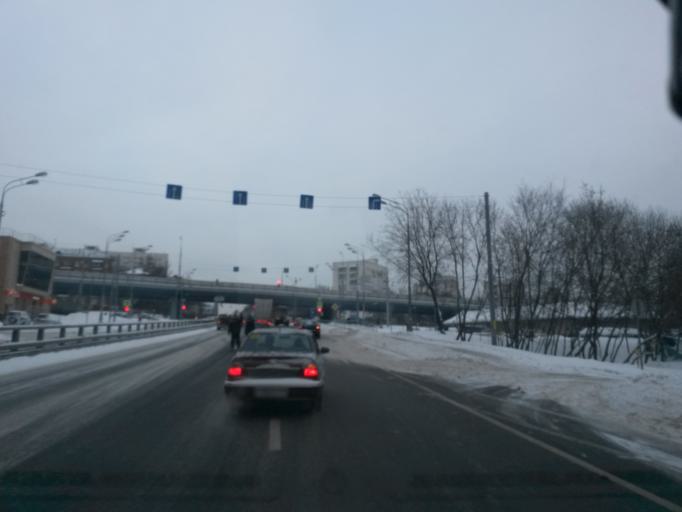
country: RU
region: Moskovskaya
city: Bol'shaya Setun'
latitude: 55.7159
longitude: 37.4087
